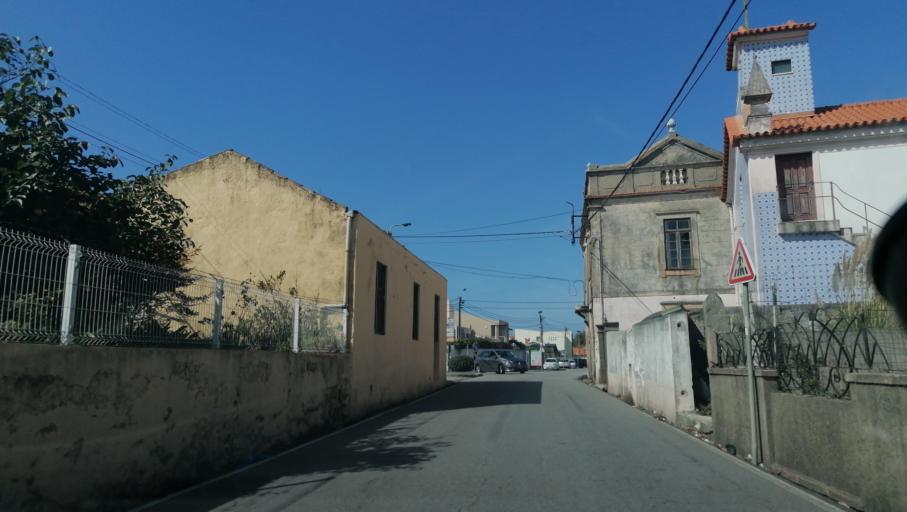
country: PT
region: Aveiro
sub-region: Espinho
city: Silvalde
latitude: 41.0036
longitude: -8.6226
